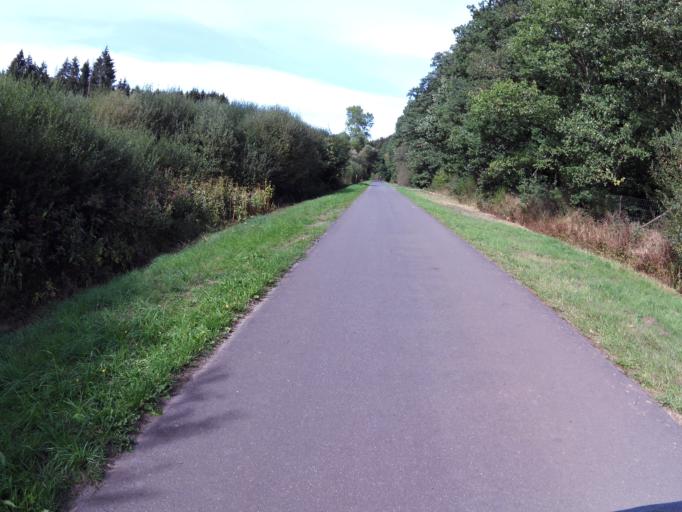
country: DE
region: Rheinland-Pfalz
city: Pronsfeld
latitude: 50.1783
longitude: 6.3157
